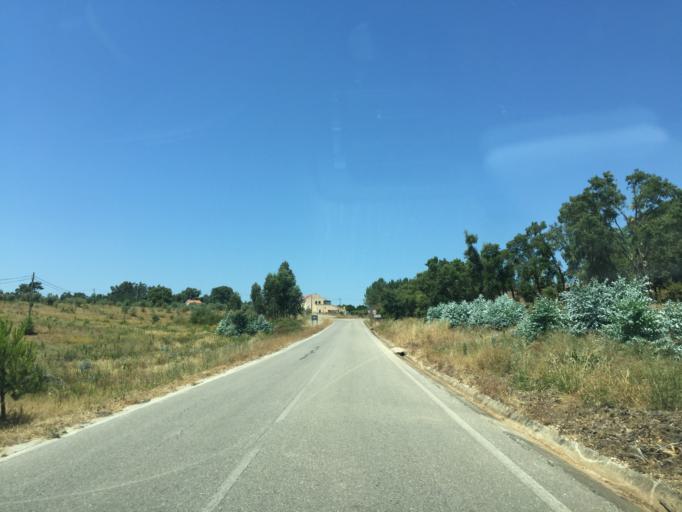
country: PT
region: Santarem
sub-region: Ferreira do Zezere
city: Ferreira do Zezere
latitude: 39.5971
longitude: -8.2912
